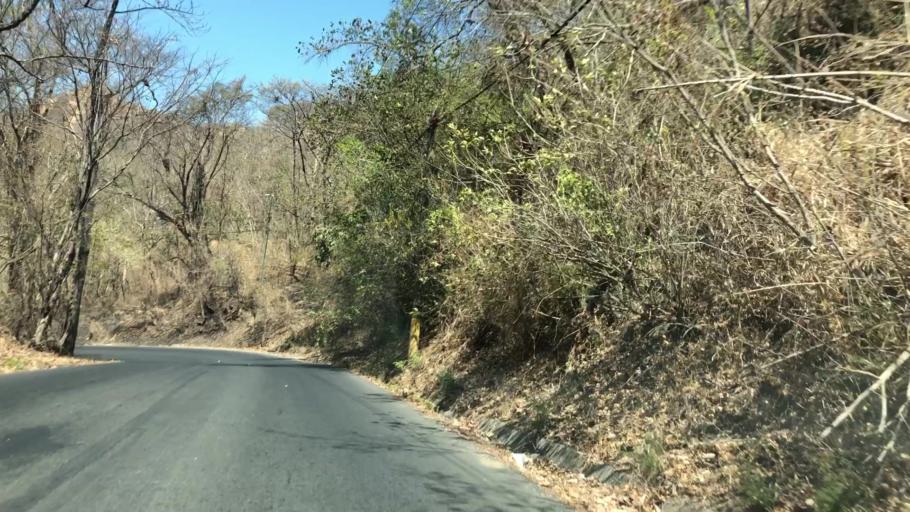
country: CR
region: Guanacaste
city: Belen
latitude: 10.3488
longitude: -85.8235
